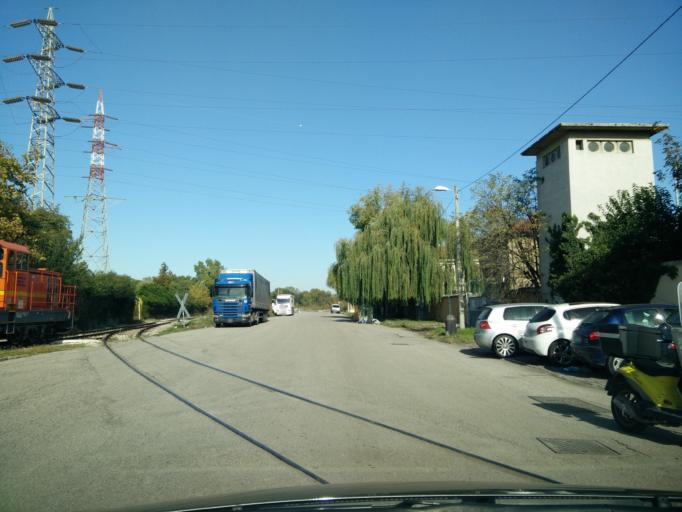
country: IT
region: Veneto
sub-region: Provincia di Venezia
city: Mestre
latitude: 45.4586
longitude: 12.2255
